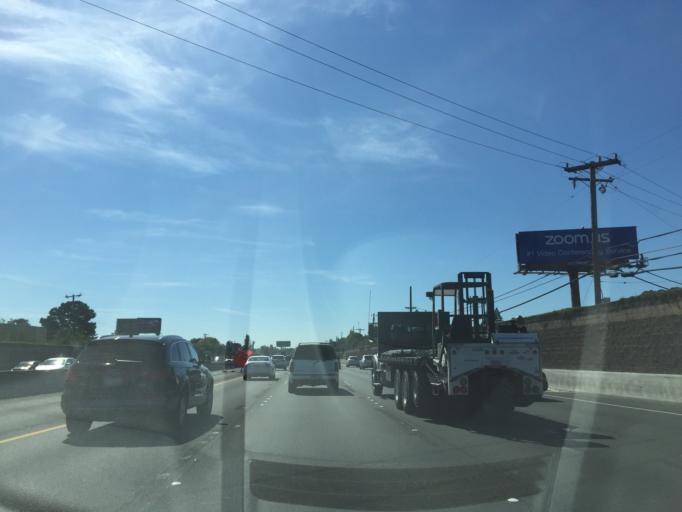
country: US
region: California
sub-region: San Mateo County
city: East Palo Alto
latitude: 37.4568
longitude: -122.1348
